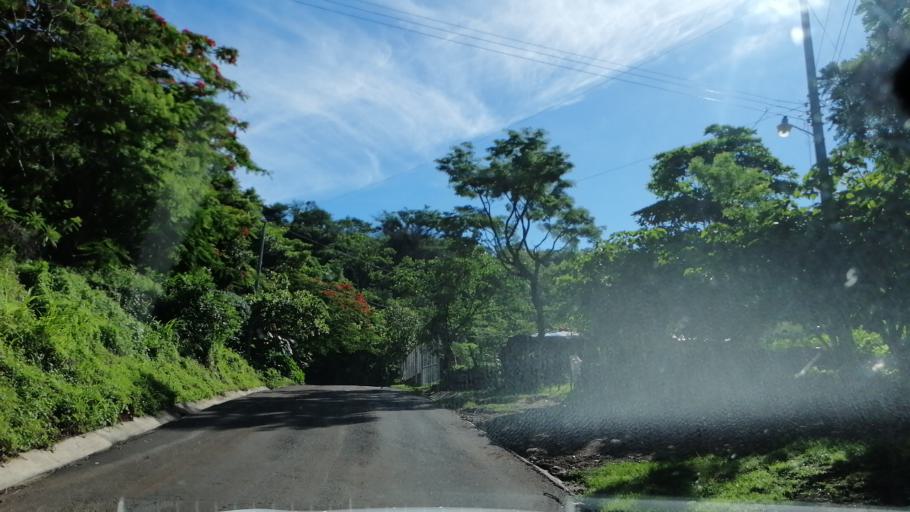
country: SV
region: Morazan
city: Corinto
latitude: 13.7954
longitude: -88.0097
